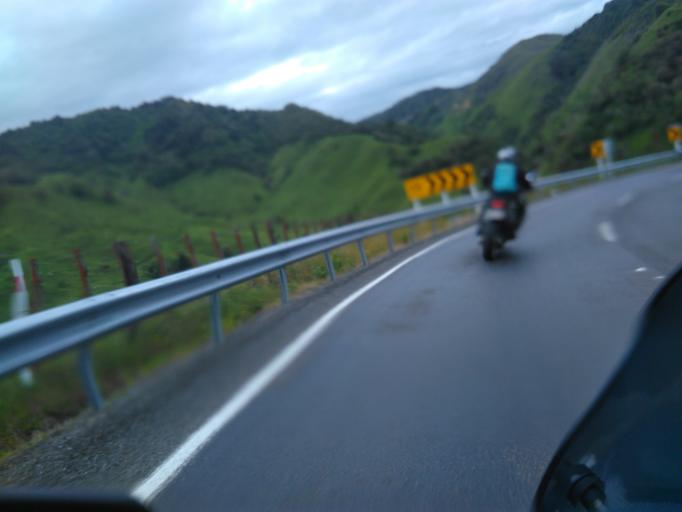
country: NZ
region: Bay of Plenty
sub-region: Opotiki District
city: Opotiki
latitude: -38.3588
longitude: 177.4584
